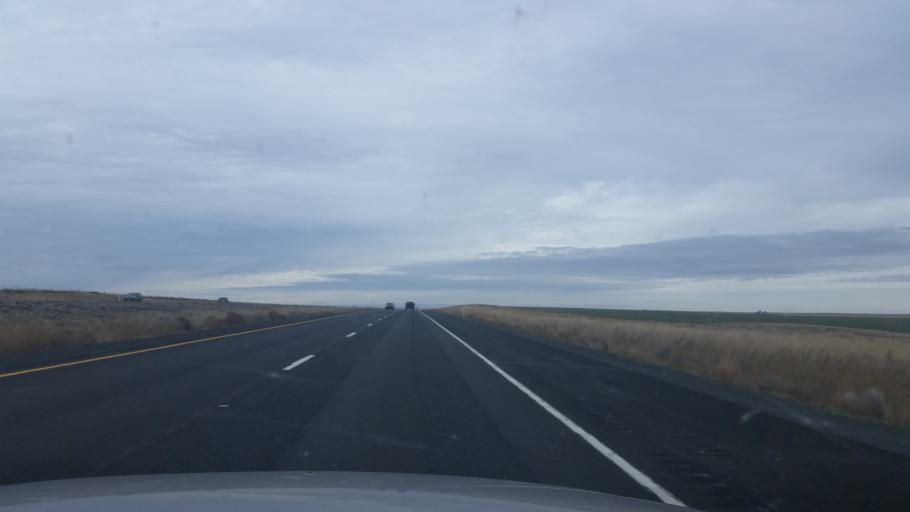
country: US
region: Washington
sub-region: Adams County
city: Ritzville
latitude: 47.1115
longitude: -118.4701
